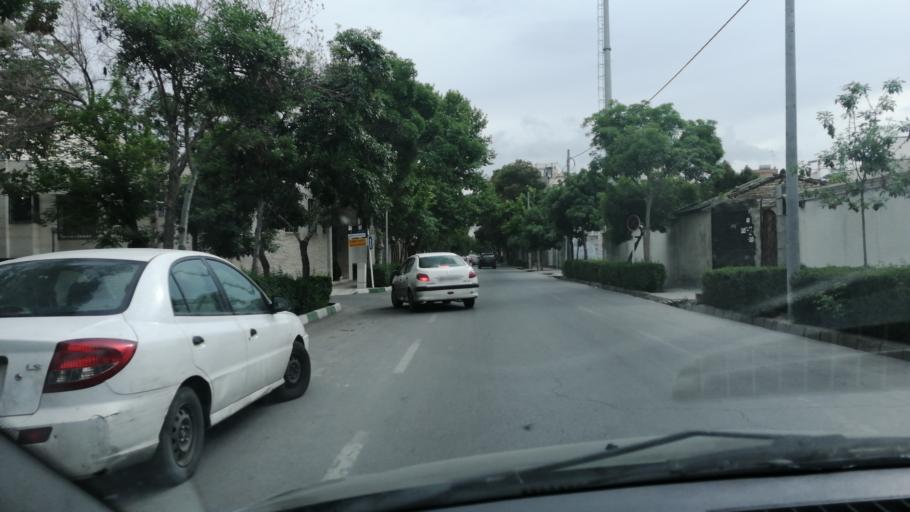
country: IR
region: Razavi Khorasan
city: Mashhad
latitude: 36.2882
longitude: 59.5858
